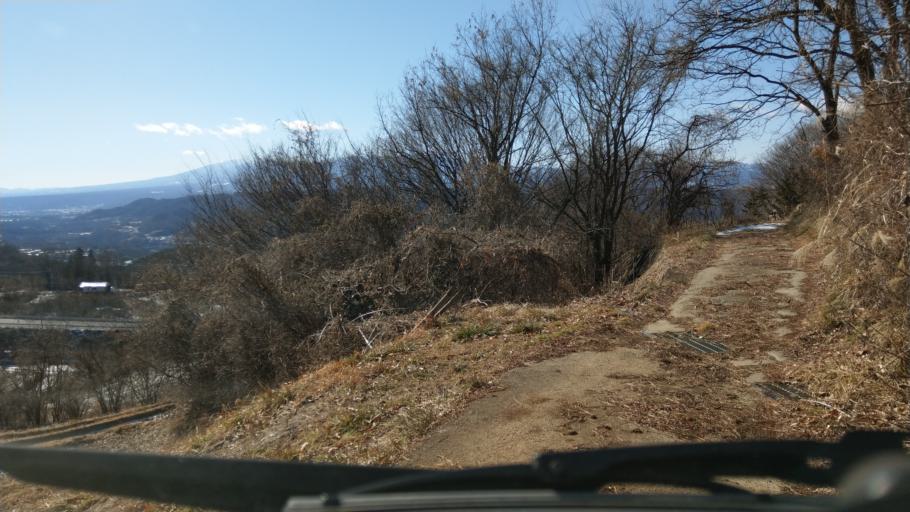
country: JP
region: Nagano
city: Komoro
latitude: 36.3536
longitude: 138.4141
